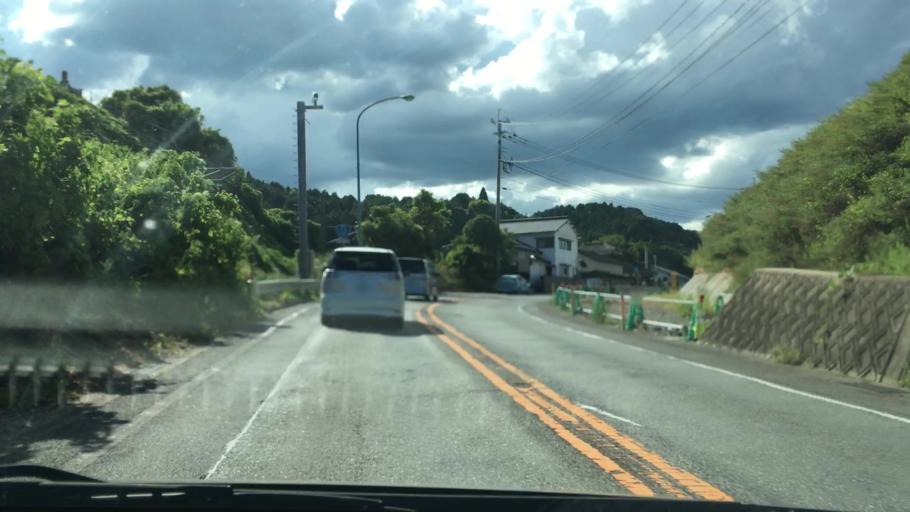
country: JP
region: Saga Prefecture
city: Takeocho-takeo
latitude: 33.1901
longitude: 129.9843
